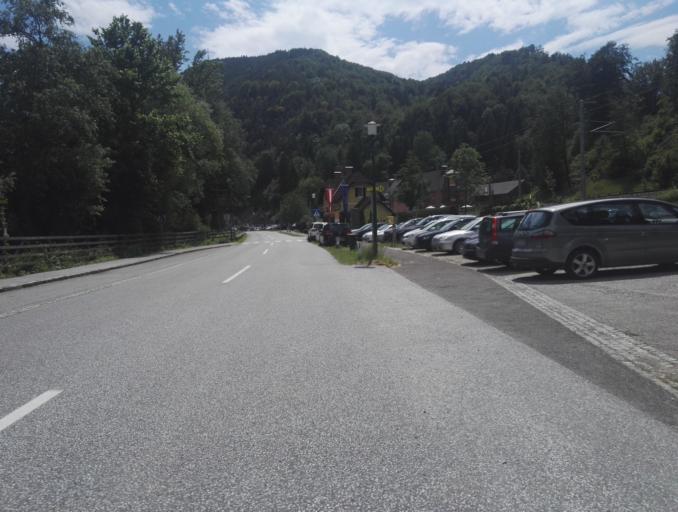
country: AT
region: Styria
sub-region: Politischer Bezirk Graz-Umgebung
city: Deutschfeistritz
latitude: 47.1597
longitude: 15.3163
